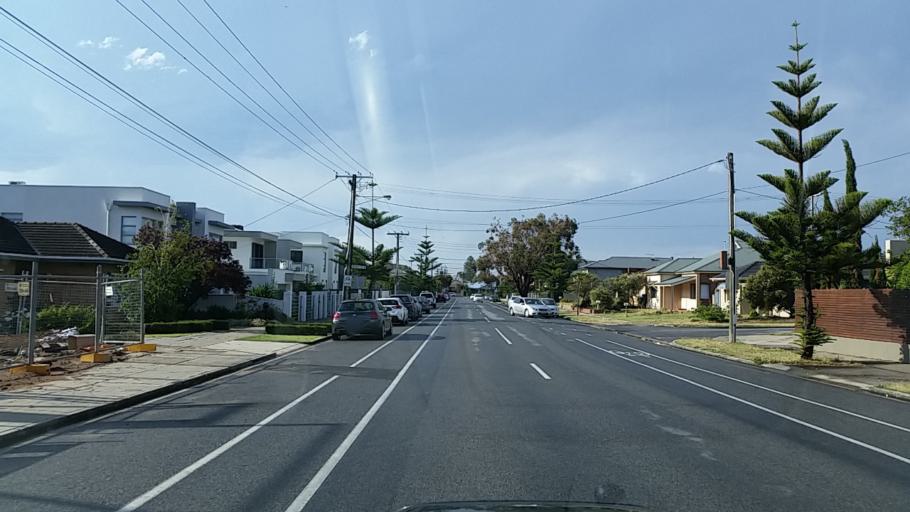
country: AU
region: South Australia
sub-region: Charles Sturt
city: Grange
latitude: -34.9096
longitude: 138.4965
